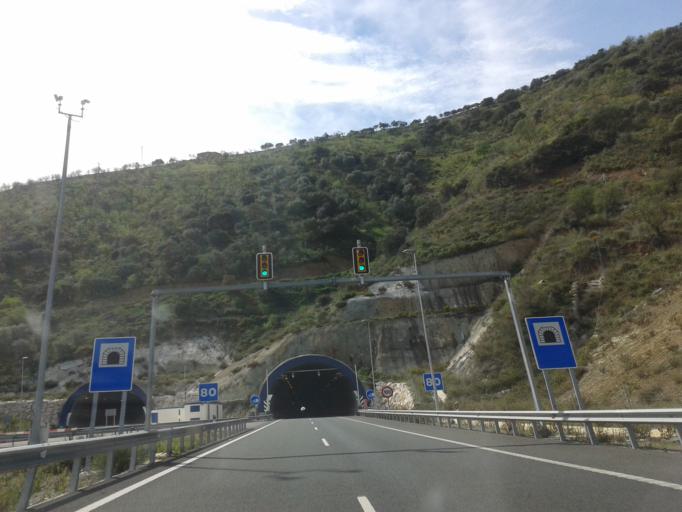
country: ES
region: Andalusia
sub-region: Provincia de Malaga
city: Casabermeja
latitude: 36.8709
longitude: -4.4834
